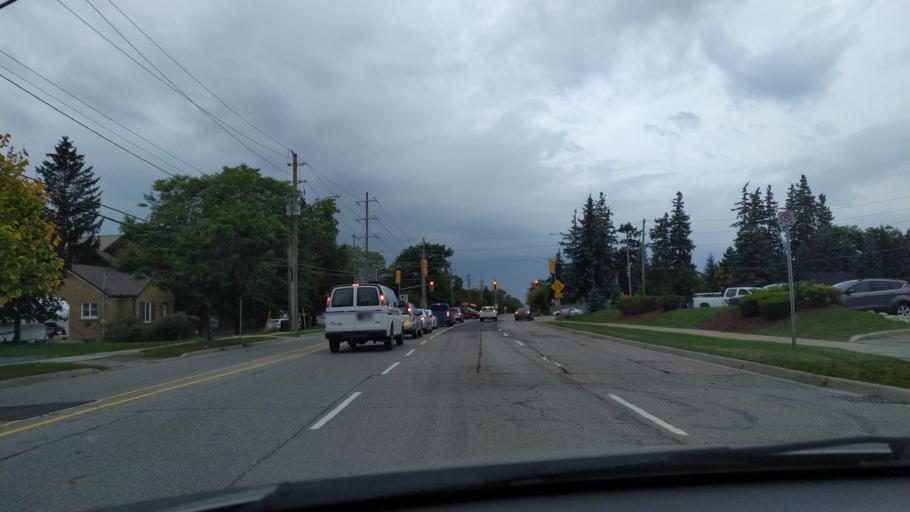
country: CA
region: Ontario
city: Waterloo
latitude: 43.4887
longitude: -80.4931
